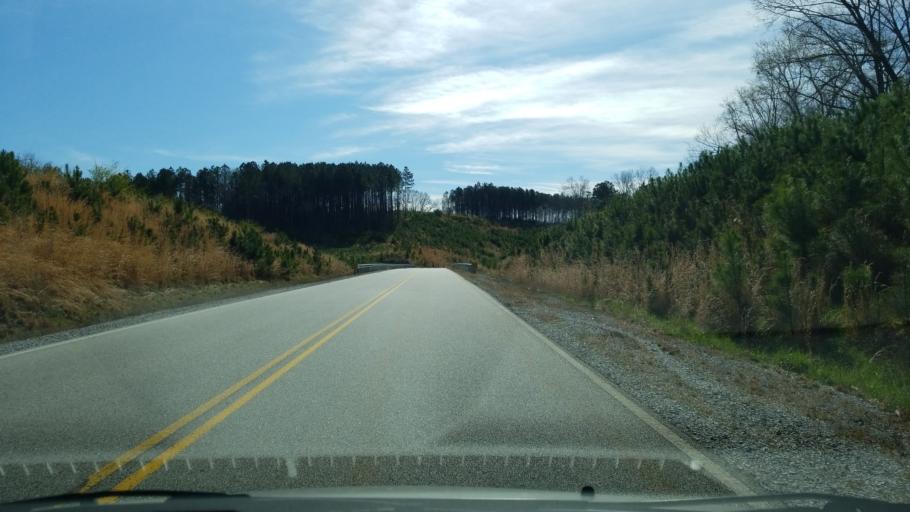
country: US
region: Tennessee
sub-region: Hamilton County
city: Harrison
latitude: 35.1046
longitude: -85.1400
